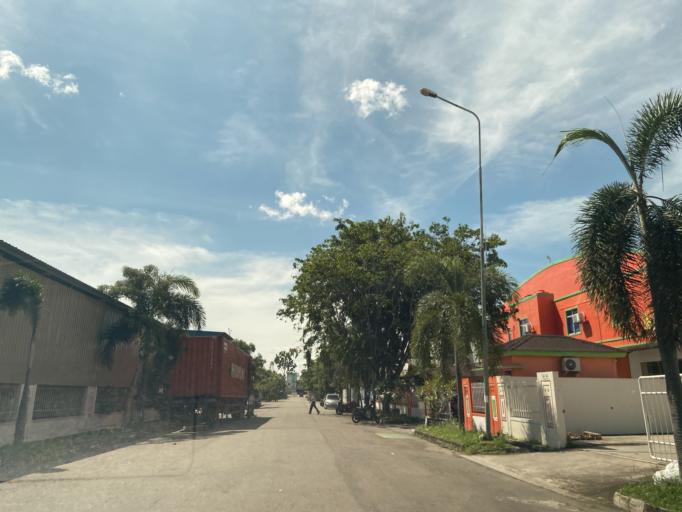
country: SG
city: Singapore
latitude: 1.1093
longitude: 104.0684
